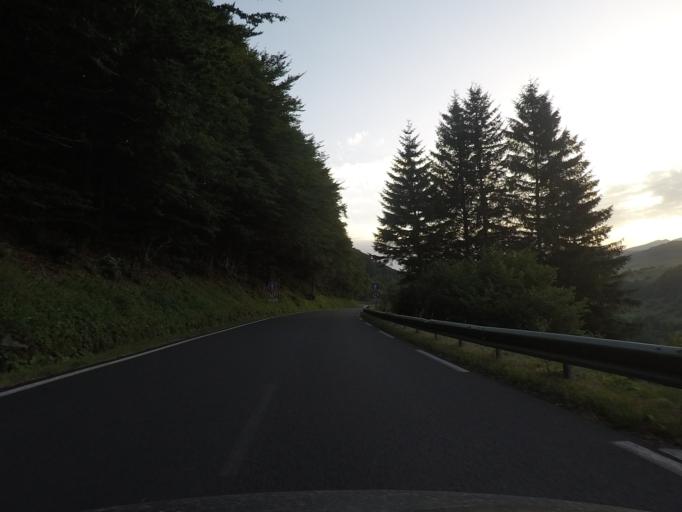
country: FR
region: Auvergne
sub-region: Departement du Puy-de-Dome
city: Mont-Dore
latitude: 45.5097
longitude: 2.9137
